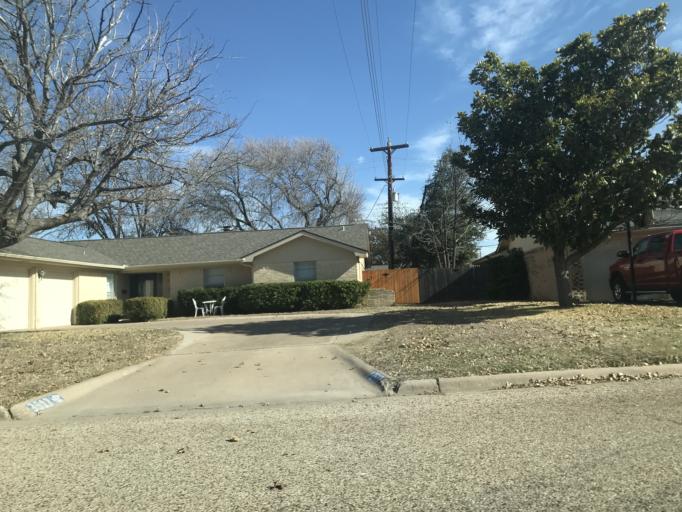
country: US
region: Texas
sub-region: Taylor County
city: Abilene
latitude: 32.4112
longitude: -99.7692
